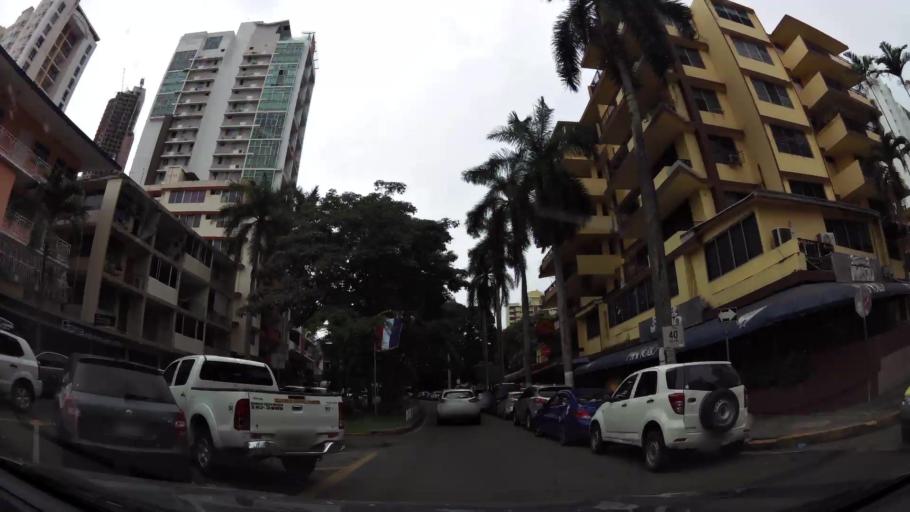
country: PA
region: Panama
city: Panama
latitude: 8.9888
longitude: -79.5254
